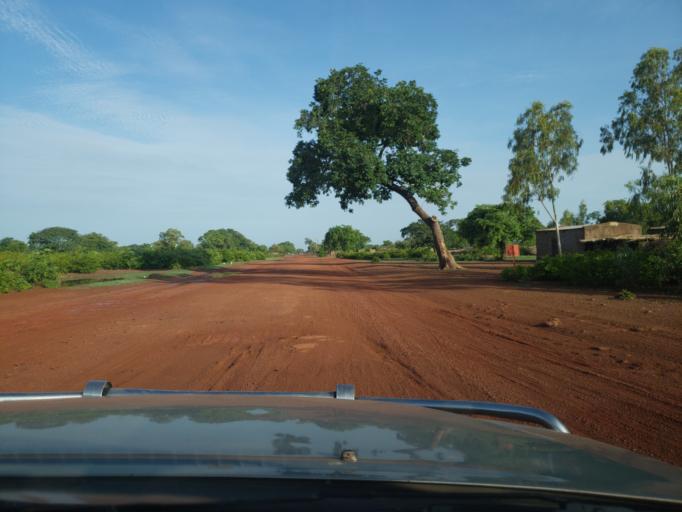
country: ML
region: Sikasso
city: Koutiala
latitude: 12.4175
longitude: -5.5741
